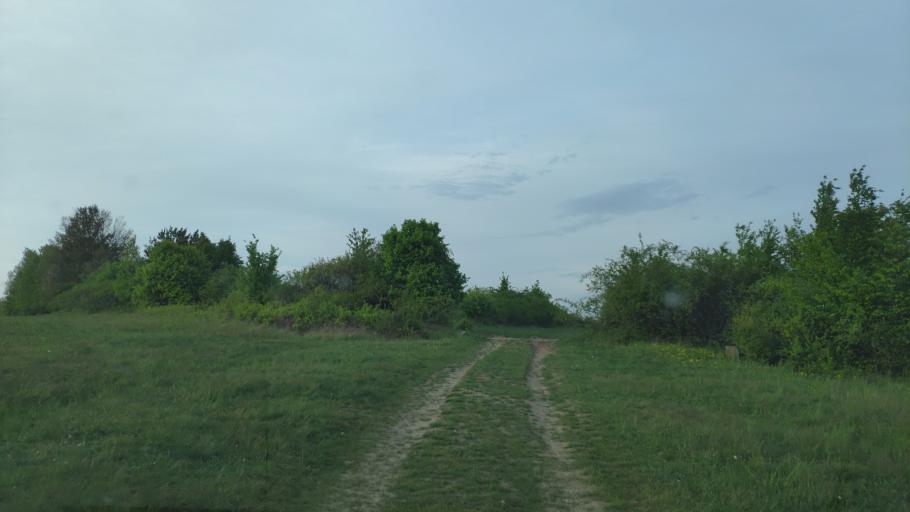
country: SK
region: Kosicky
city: Kosice
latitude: 48.7223
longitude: 21.3612
